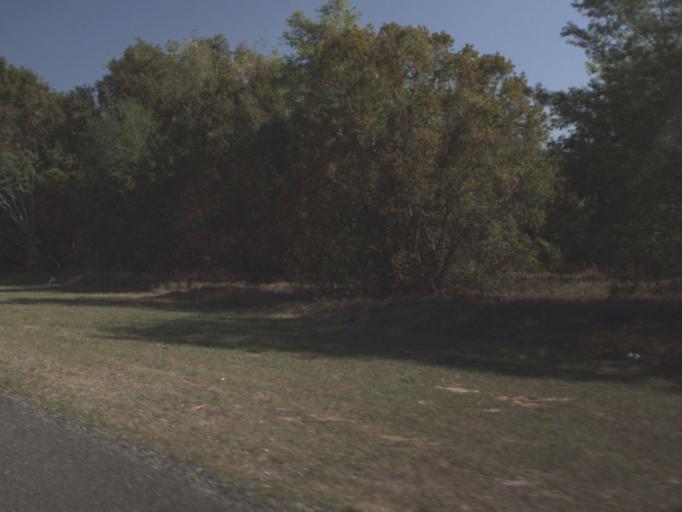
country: US
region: Florida
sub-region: Lake County
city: Minneola
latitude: 28.6020
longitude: -81.7550
